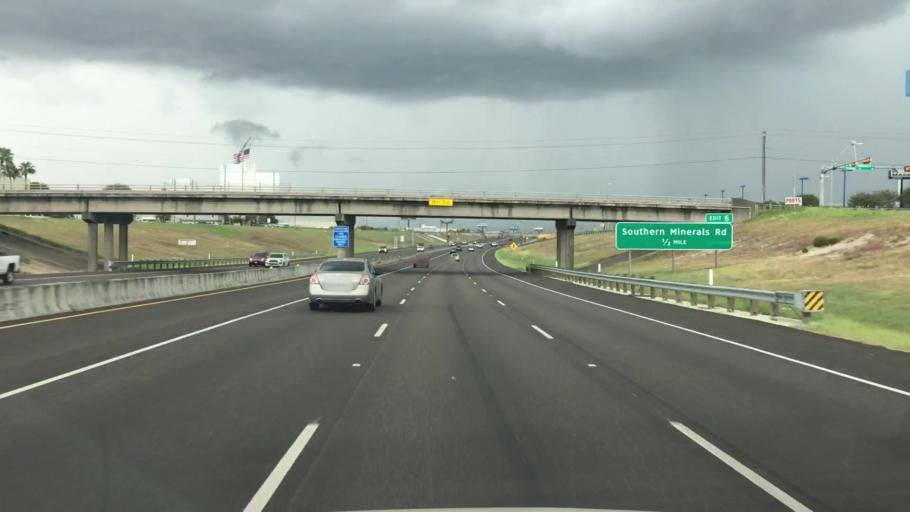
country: US
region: Texas
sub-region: Nueces County
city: Corpus Christi
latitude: 27.8051
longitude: -97.4838
